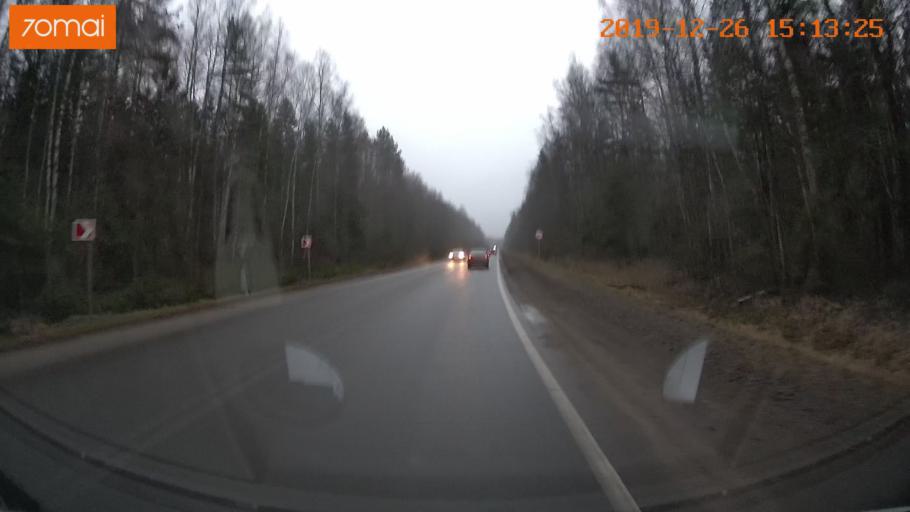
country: RU
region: Jaroslavl
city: Rybinsk
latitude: 58.1171
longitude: 38.8837
